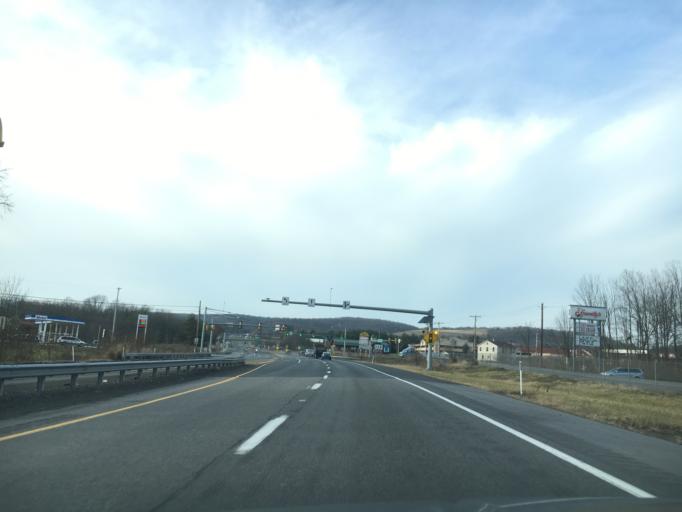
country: US
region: Pennsylvania
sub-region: Northumberland County
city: Riverside
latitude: 40.9940
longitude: -76.6391
